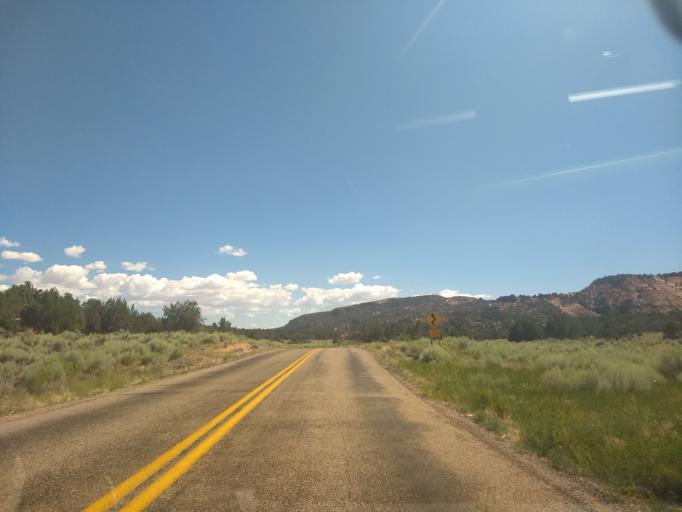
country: US
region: Utah
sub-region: Washington County
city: Hildale
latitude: 36.9998
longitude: -112.8619
